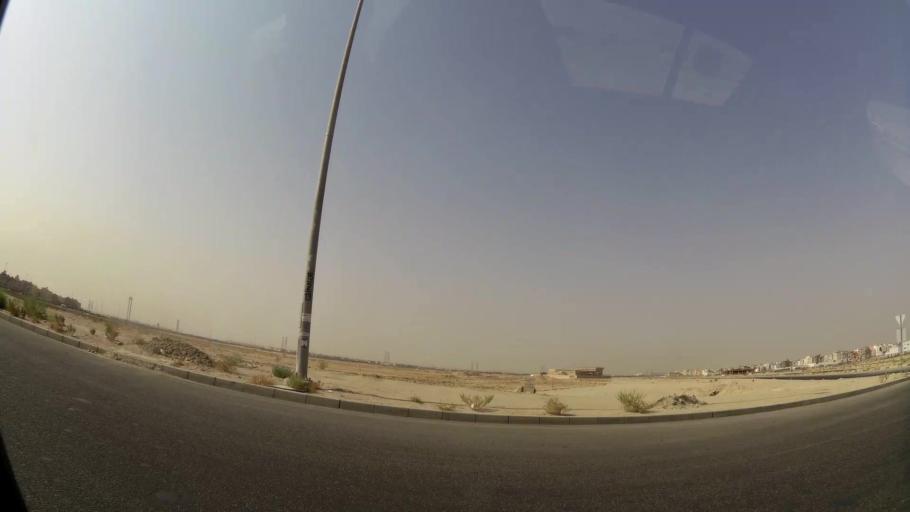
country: KW
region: Muhafazat al Jahra'
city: Al Jahra'
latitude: 29.3417
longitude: 47.7606
